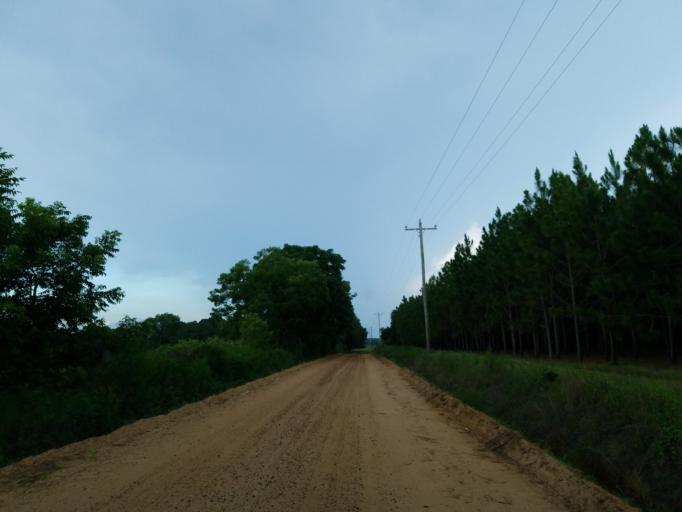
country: US
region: Georgia
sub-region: Tift County
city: Omega
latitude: 31.2748
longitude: -83.5244
